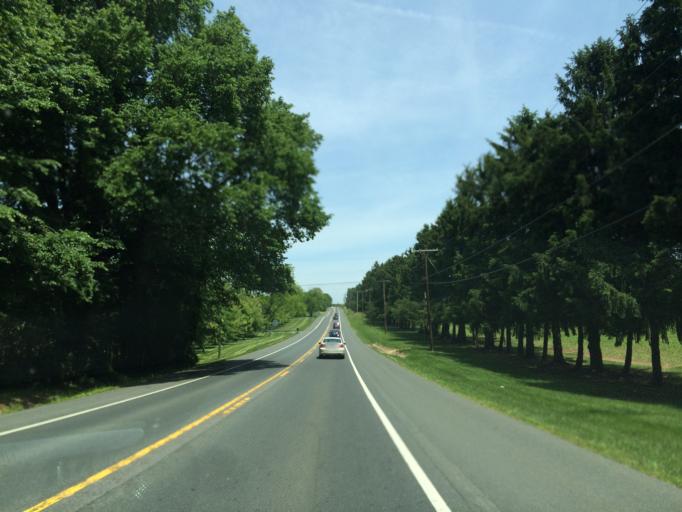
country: US
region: Maryland
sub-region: Washington County
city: Saint James
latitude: 39.5593
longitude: -77.7333
